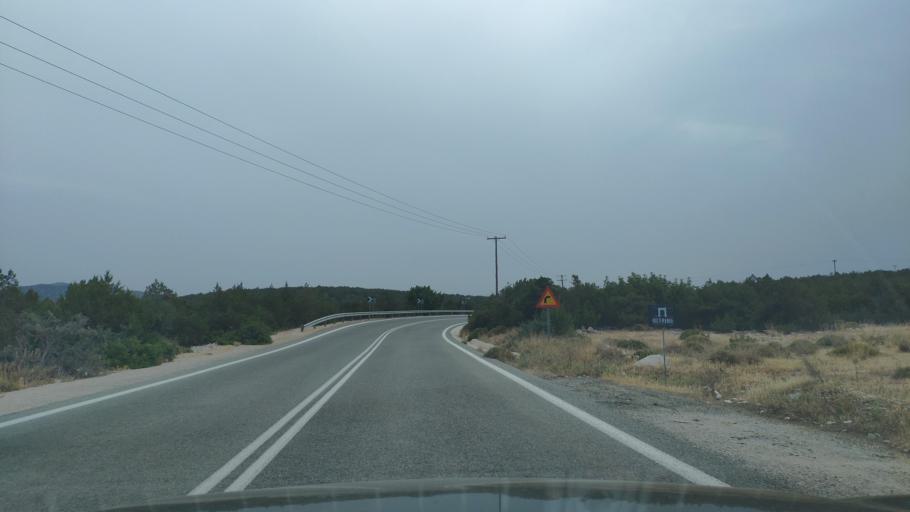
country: GR
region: Peloponnese
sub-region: Nomos Argolidos
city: Didyma
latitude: 37.4514
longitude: 23.1946
